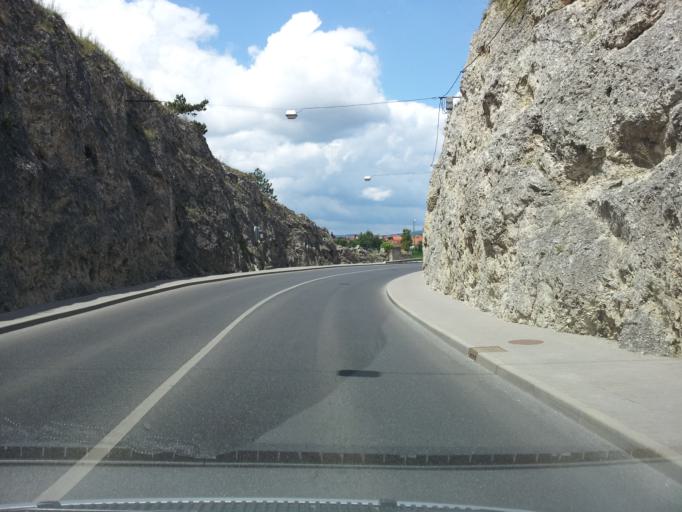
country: HU
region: Veszprem
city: Veszprem
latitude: 47.0960
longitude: 17.8971
